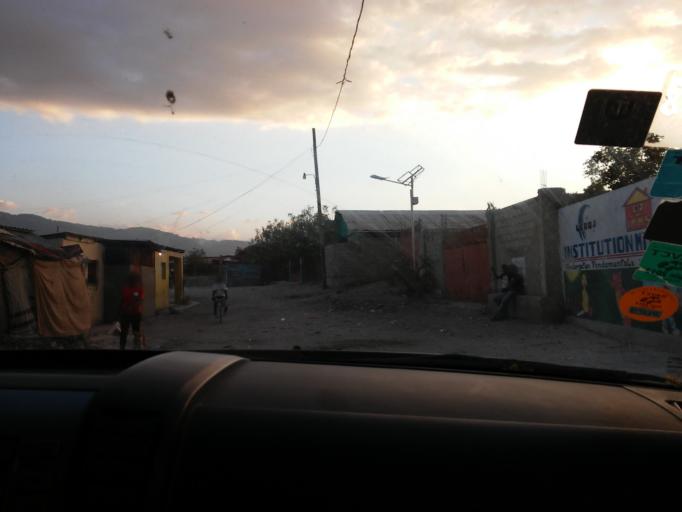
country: HT
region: Ouest
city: Port-au-Prince
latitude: 18.5673
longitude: -72.3504
